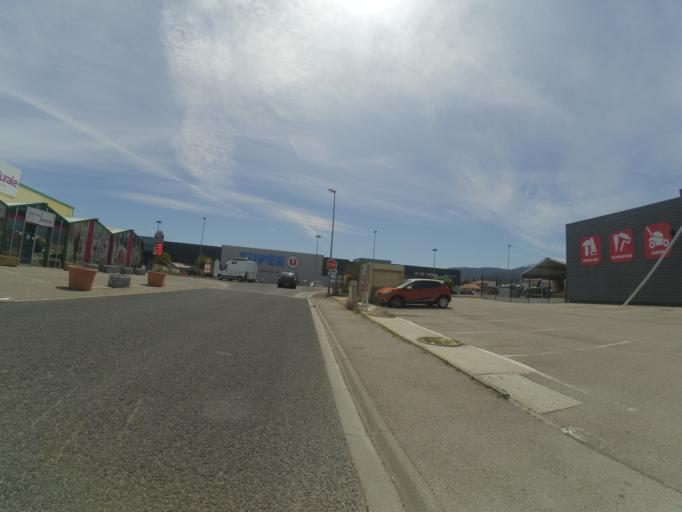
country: FR
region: Languedoc-Roussillon
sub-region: Departement des Pyrenees-Orientales
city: Ille-sur-Tet
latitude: 42.6770
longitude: 2.6330
